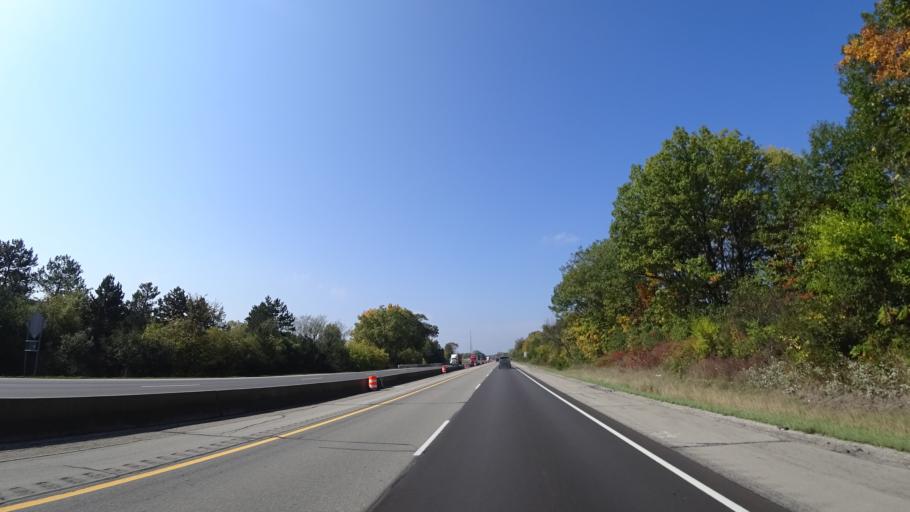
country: US
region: Michigan
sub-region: Washtenaw County
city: Ann Arbor
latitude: 42.2856
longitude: -83.7913
